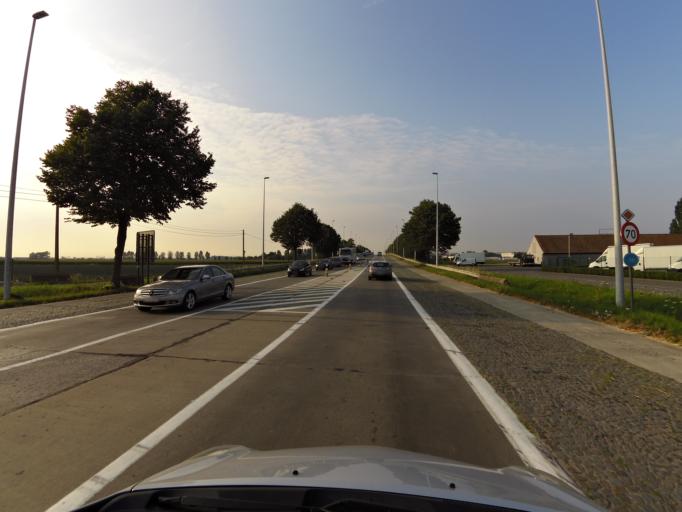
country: BE
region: Flanders
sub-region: Provincie West-Vlaanderen
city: Lichtervelde
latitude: 51.0254
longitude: 3.1112
